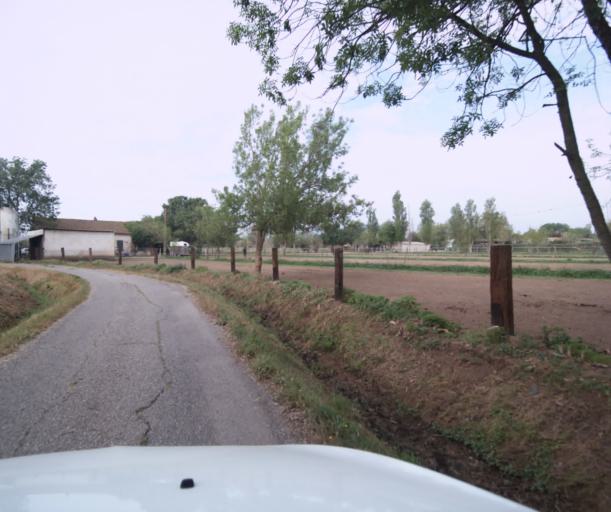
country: FR
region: Provence-Alpes-Cote d'Azur
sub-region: Departement du Var
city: Hyeres
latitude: 43.1098
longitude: 6.1633
